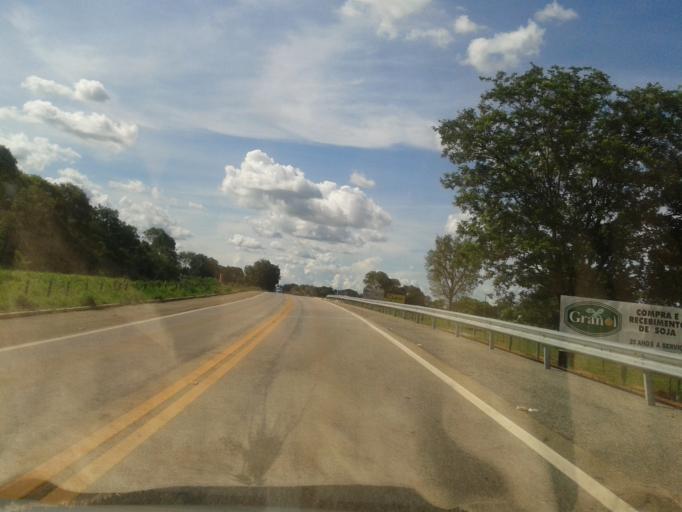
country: BR
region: Goias
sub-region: Mozarlandia
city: Mozarlandia
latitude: -15.1077
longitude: -50.6084
